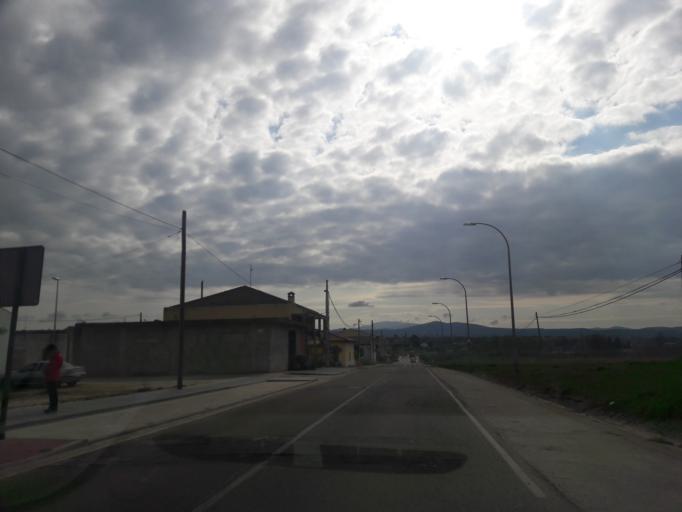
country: ES
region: Castille and Leon
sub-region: Provincia de Salamanca
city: Ciudad Rodrigo
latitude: 40.5957
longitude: -6.5223
